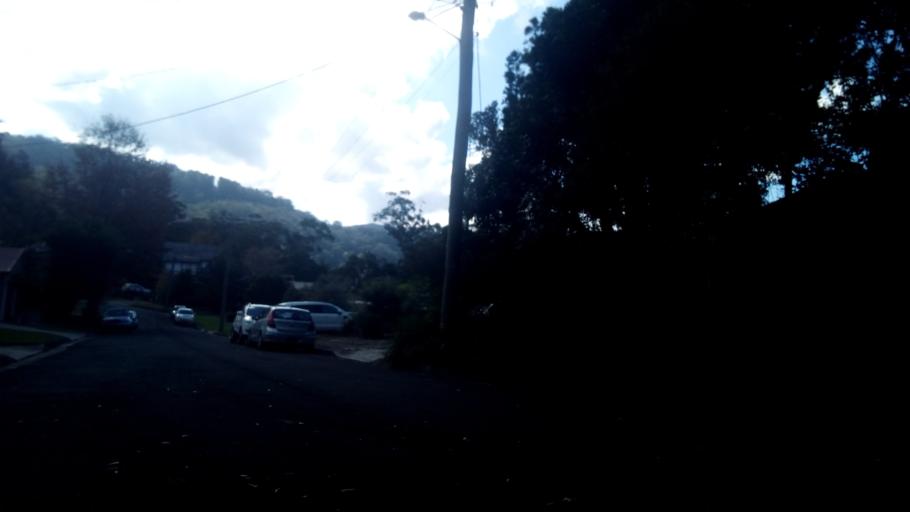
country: AU
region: New South Wales
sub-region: Wollongong
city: Cordeaux Heights
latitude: -34.4340
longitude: 150.8156
